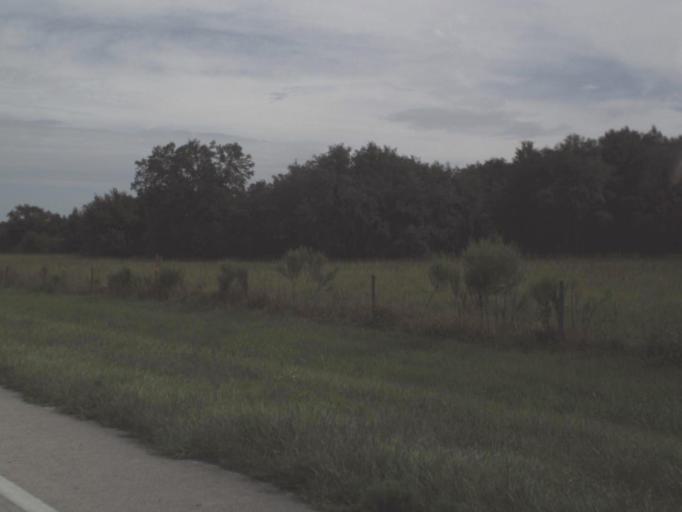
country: US
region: Florida
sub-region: DeSoto County
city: Southeast Arcadia
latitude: 27.1288
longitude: -81.7962
